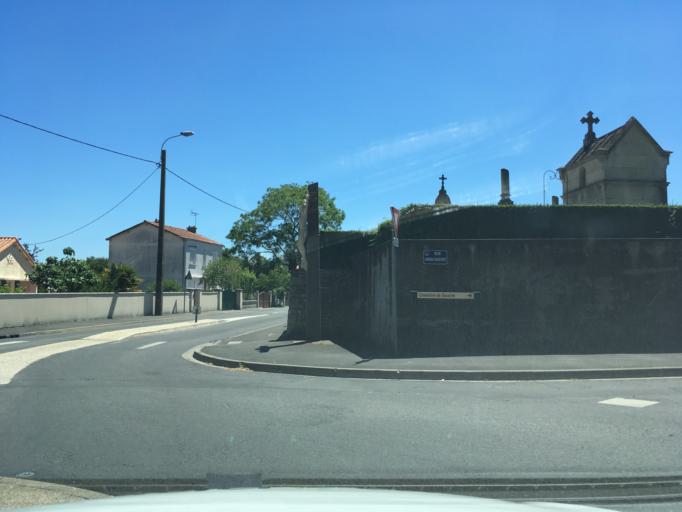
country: FR
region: Poitou-Charentes
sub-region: Departement des Deux-Sevres
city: Aiffres
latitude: 46.3245
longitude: -0.4251
